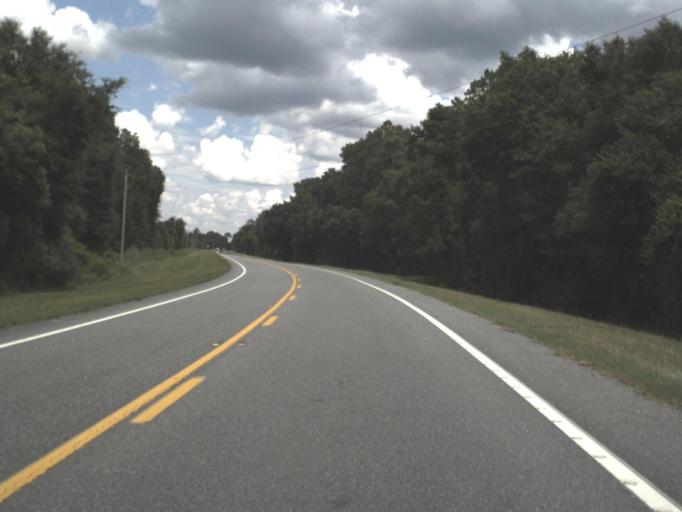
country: US
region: Florida
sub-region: Taylor County
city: Perry
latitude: 30.0828
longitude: -83.5011
